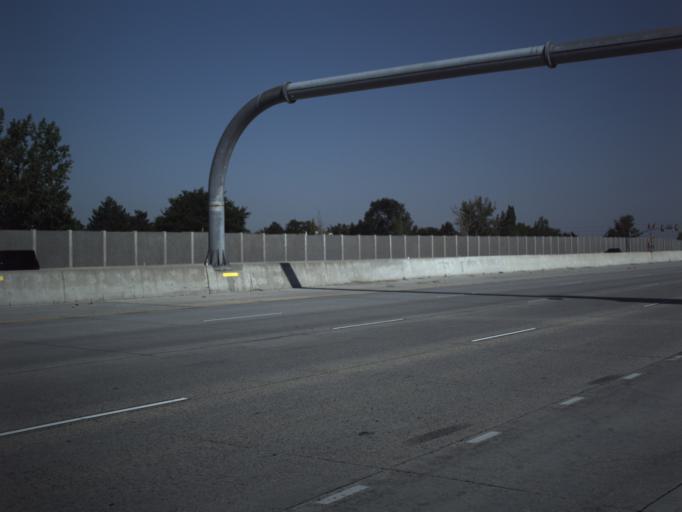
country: US
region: Utah
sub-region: Salt Lake County
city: Taylorsville
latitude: 40.6626
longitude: -111.9523
